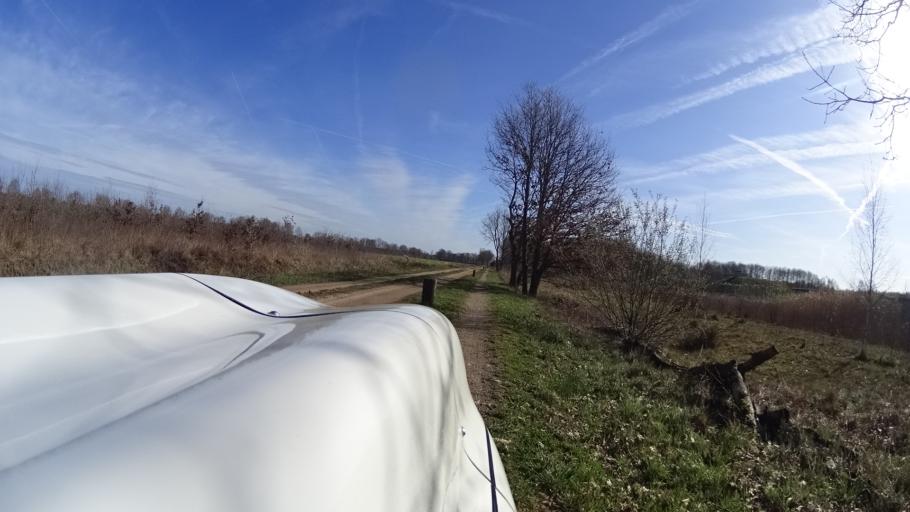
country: NL
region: North Brabant
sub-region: Gemeente Uden
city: Odiliapeel
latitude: 51.6663
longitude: 5.6995
